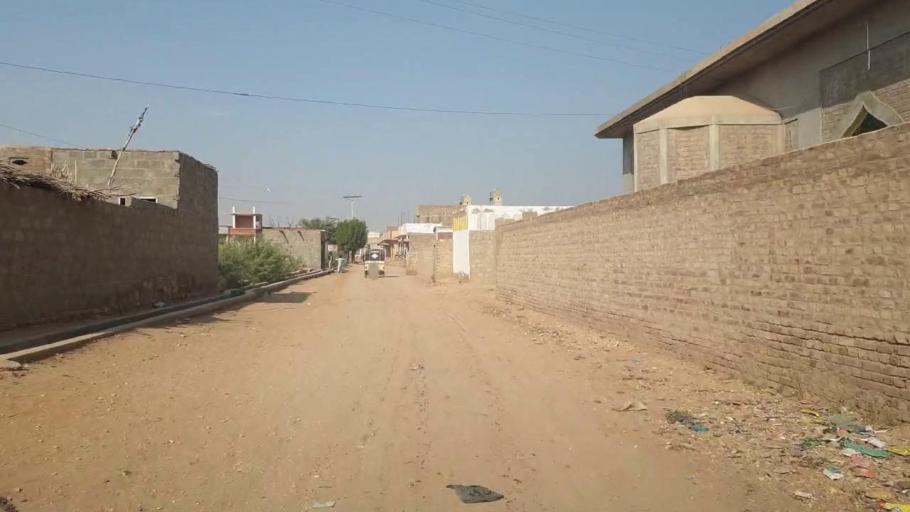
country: PK
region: Sindh
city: Jamshoro
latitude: 25.4400
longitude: 68.2814
